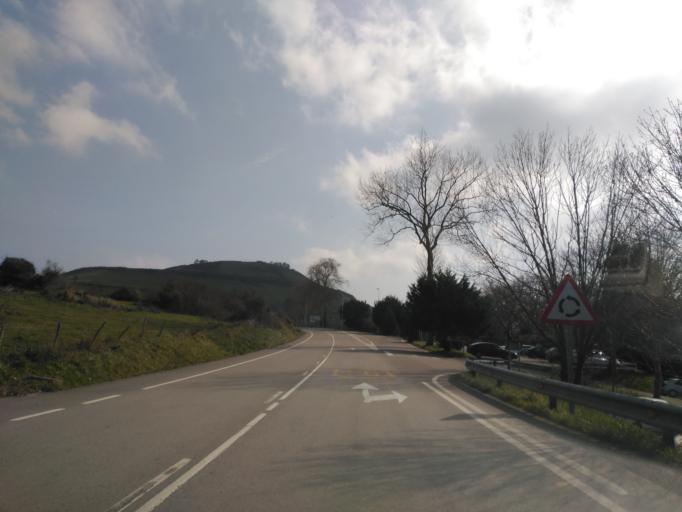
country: ES
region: Cantabria
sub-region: Provincia de Cantabria
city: Santillana
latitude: 43.3824
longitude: -4.1042
